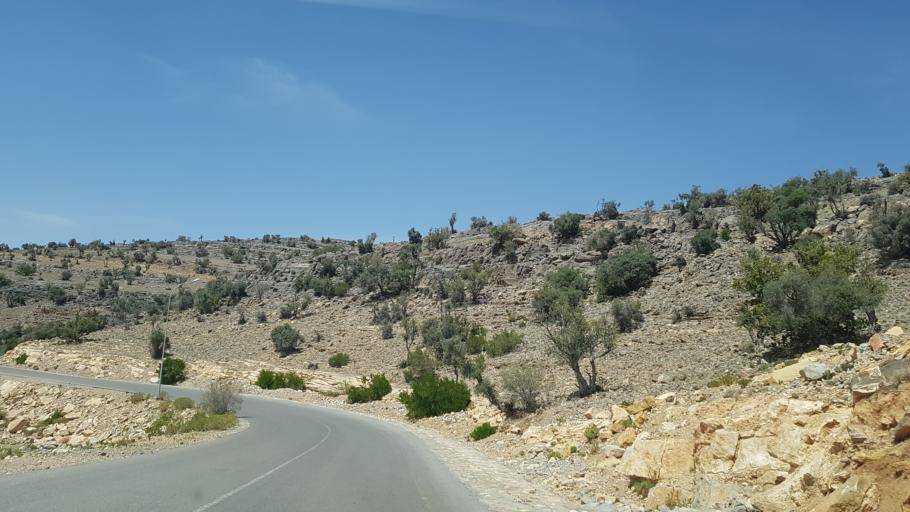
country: OM
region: Al Batinah
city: Bayt al `Awabi
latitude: 23.1377
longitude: 57.5949
